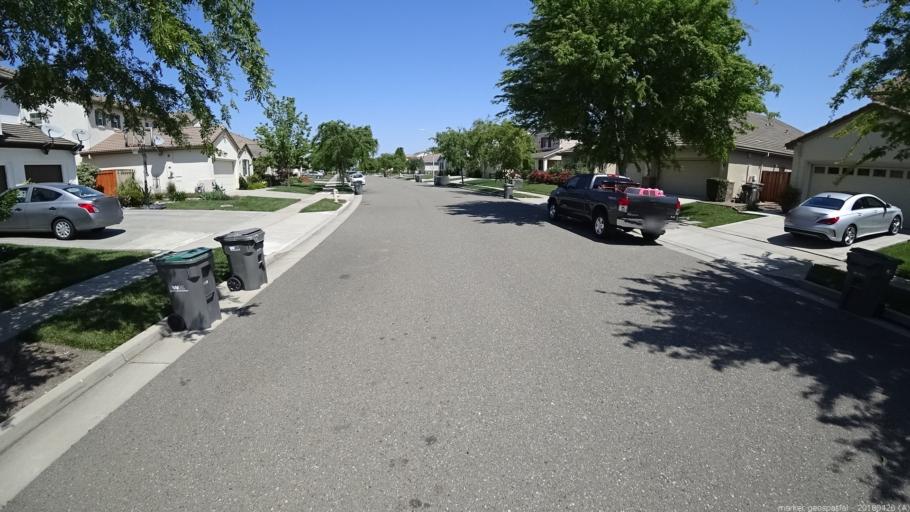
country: US
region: California
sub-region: Yolo County
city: West Sacramento
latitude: 38.5285
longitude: -121.5811
